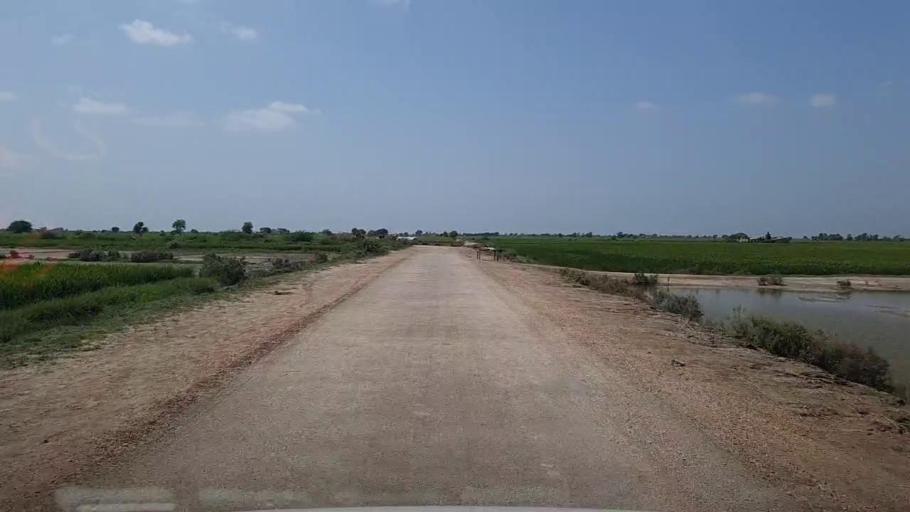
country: PK
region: Sindh
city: Kario
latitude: 24.8236
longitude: 68.6997
